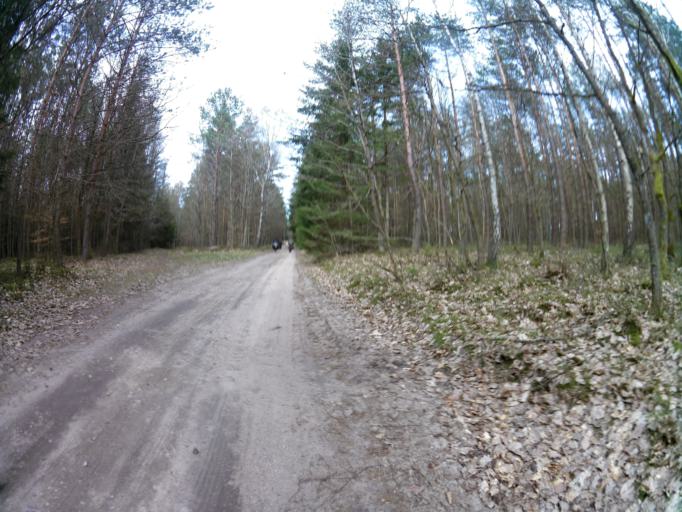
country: PL
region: West Pomeranian Voivodeship
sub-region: Powiat szczecinecki
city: Szczecinek
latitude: 53.8233
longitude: 16.6505
